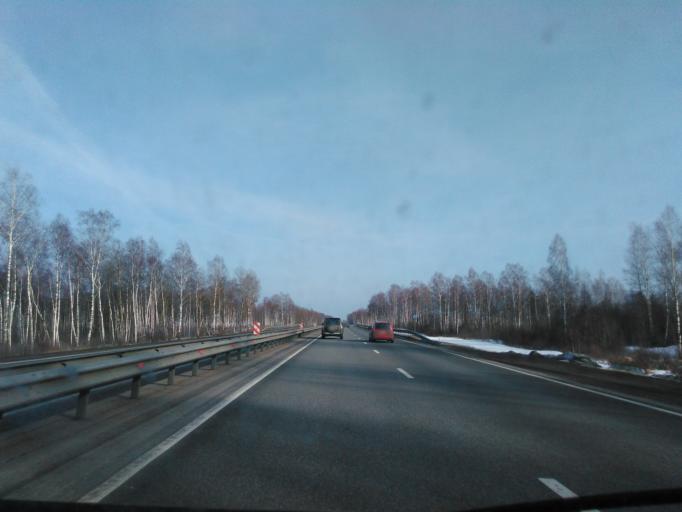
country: RU
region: Smolensk
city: Verkhnedneprovskiy
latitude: 55.1816
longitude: 33.5751
